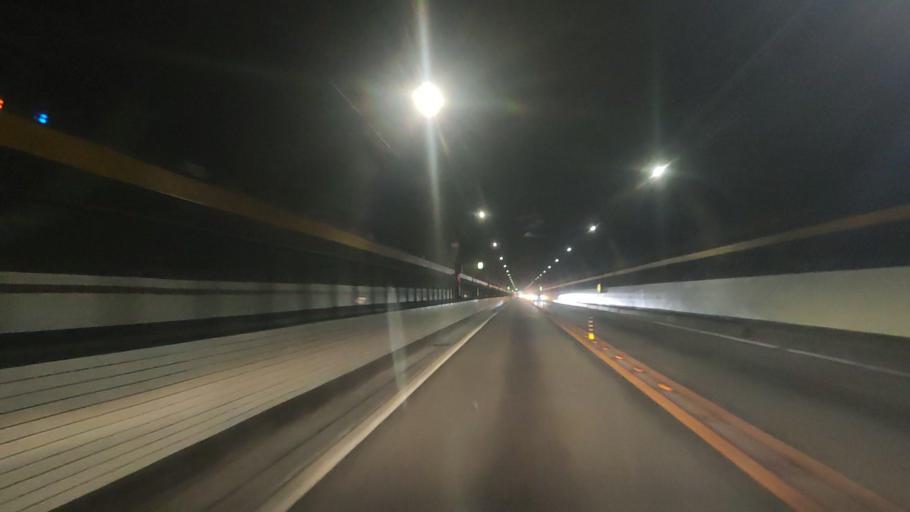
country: JP
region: Nagasaki
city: Obita
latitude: 32.7805
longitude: 129.8859
